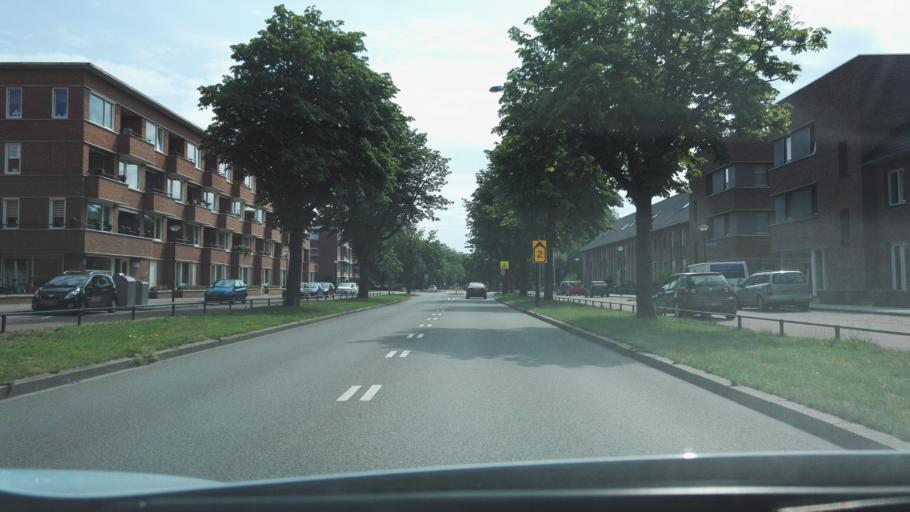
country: NL
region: Gelderland
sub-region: Gemeente Apeldoorn
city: Apeldoorn
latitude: 52.1942
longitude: 5.9682
